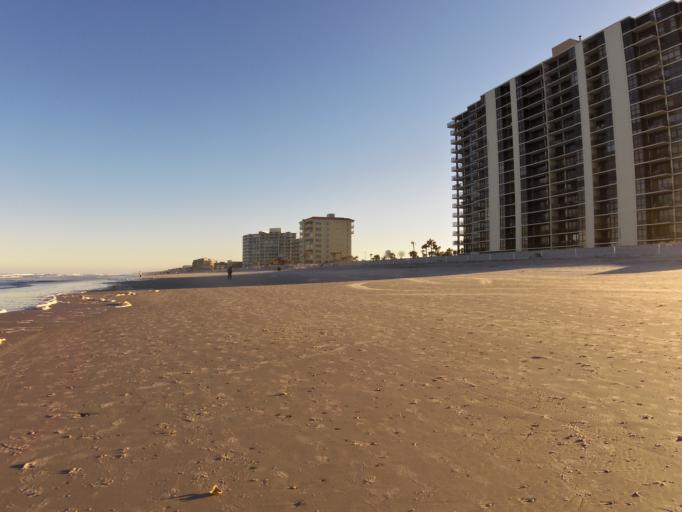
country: US
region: Florida
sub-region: Duval County
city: Jacksonville Beach
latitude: 30.2770
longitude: -81.3856
